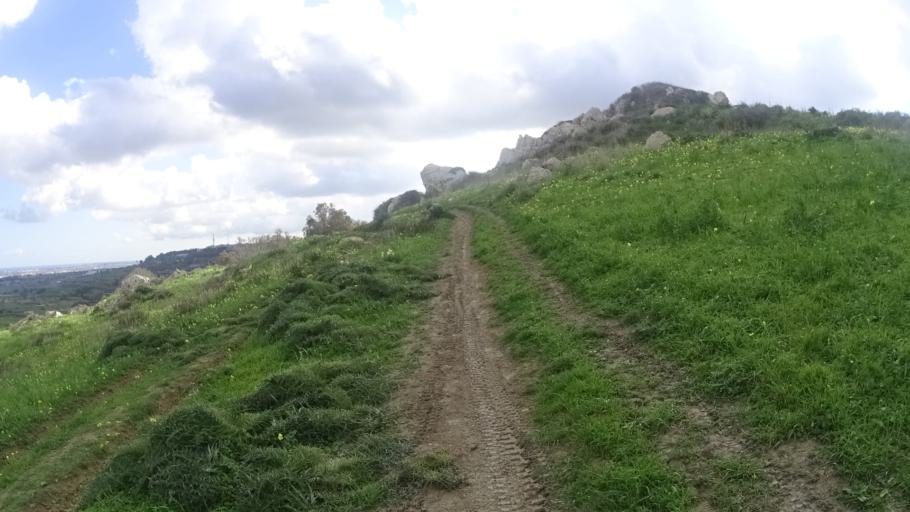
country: MT
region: L-Imtarfa
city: Imtarfa
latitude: 35.8999
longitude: 14.3849
